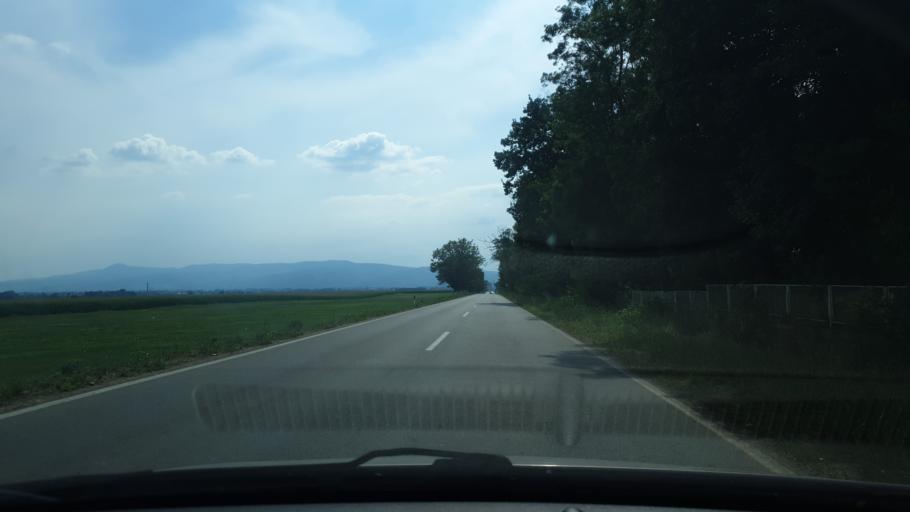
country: RS
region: Central Serbia
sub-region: Pomoravski Okrug
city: Cuprija
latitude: 43.9421
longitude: 21.4122
